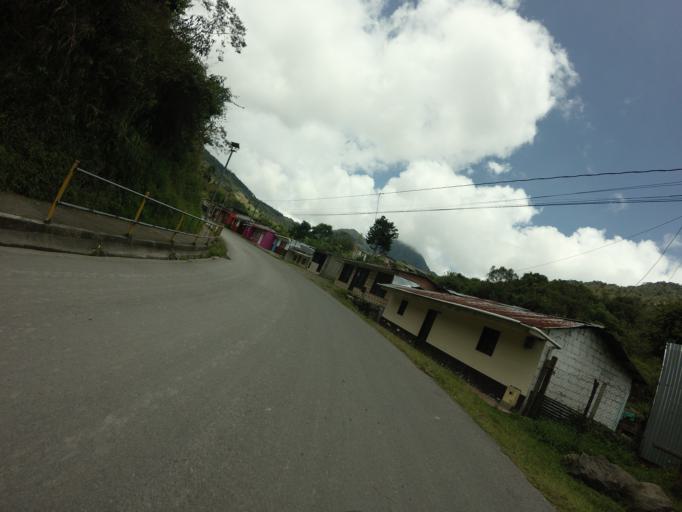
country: CO
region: Caldas
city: Manzanares
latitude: 5.2591
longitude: -75.1477
